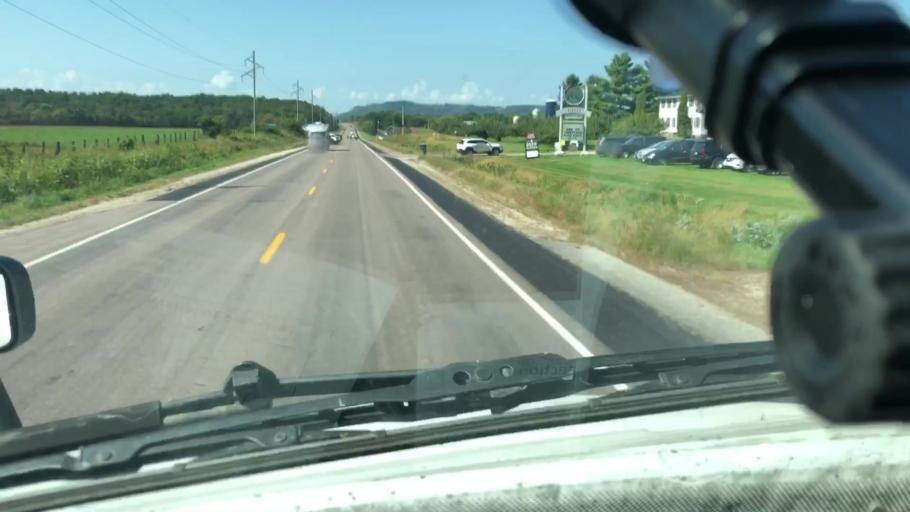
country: US
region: Wisconsin
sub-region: Trempealeau County
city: Trempealeau
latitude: 44.0700
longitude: -91.4915
